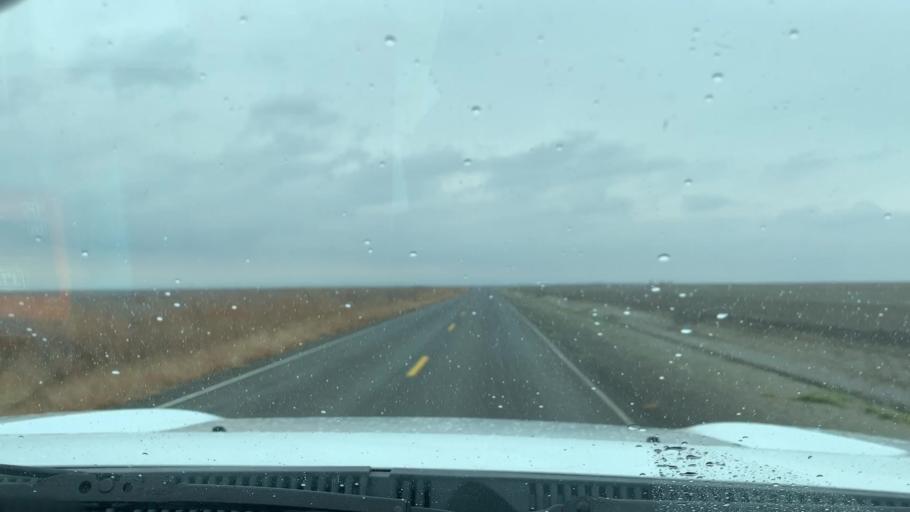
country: US
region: California
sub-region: Kings County
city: Kettleman City
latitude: 35.9340
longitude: -119.7477
